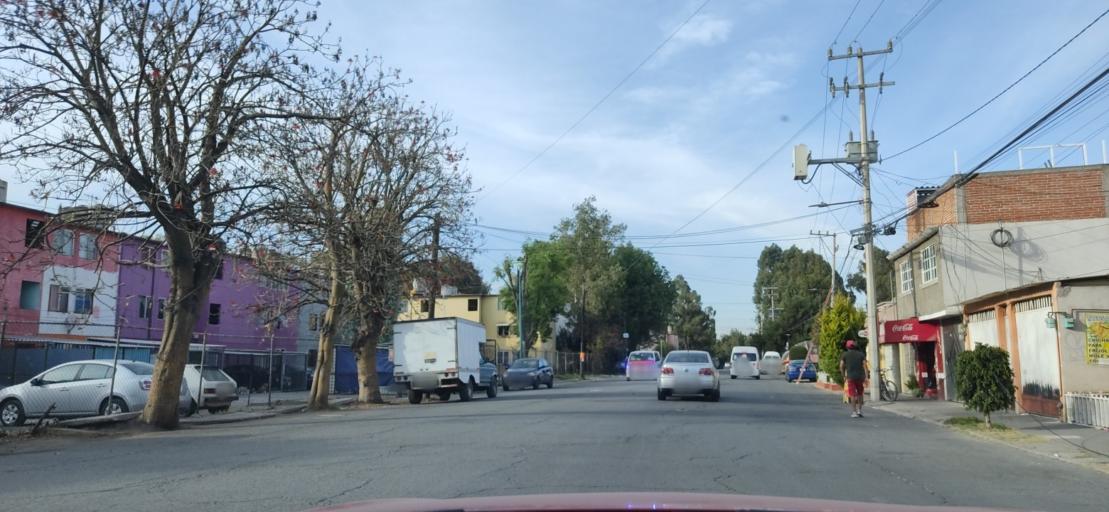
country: MX
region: Mexico
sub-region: Cuautitlan
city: San Jose del Puente
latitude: 19.6914
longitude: -99.2072
